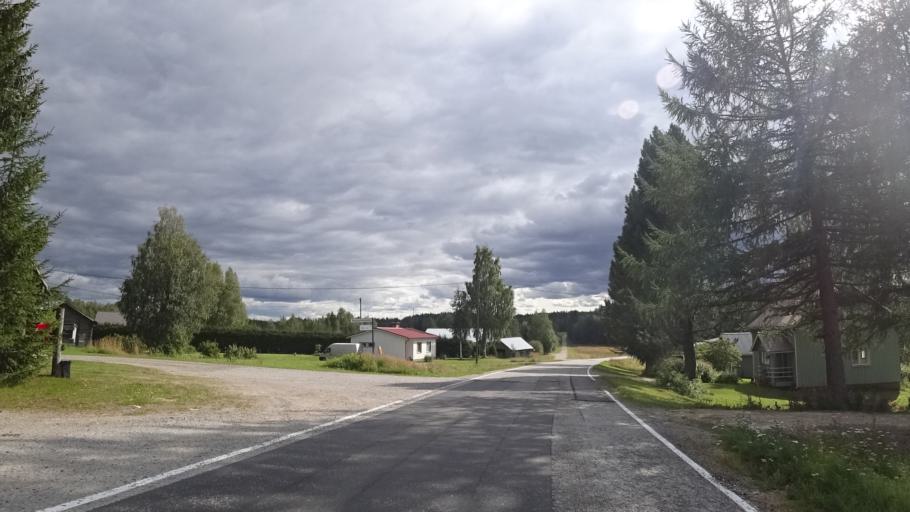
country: FI
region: North Karelia
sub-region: Joensuu
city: Ilomantsi
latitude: 62.4491
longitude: 31.1153
